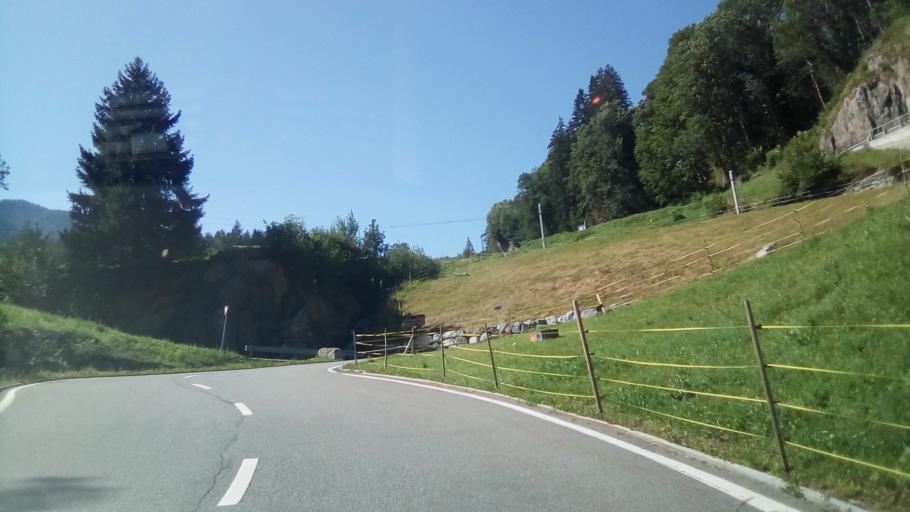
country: CH
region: Valais
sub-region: Saint-Maurice District
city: Salvan
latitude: 46.1160
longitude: 7.0145
